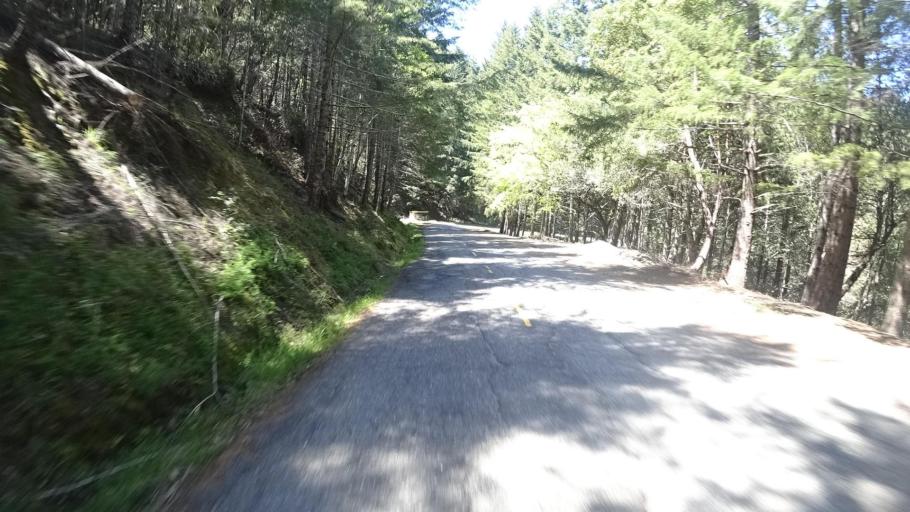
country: US
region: California
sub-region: Humboldt County
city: Rio Dell
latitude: 40.3179
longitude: -124.0610
